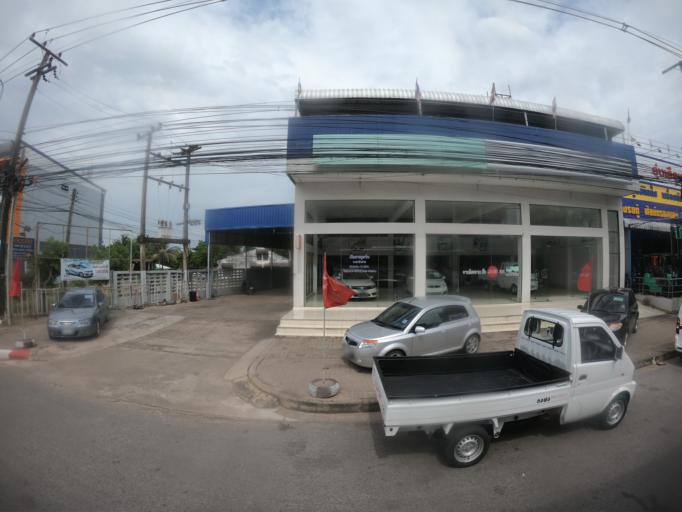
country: TH
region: Roi Et
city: Roi Et
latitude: 16.0566
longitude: 103.6367
